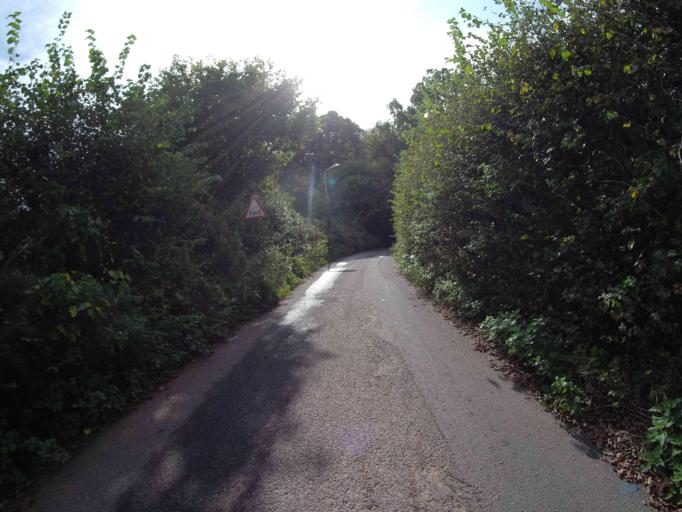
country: GB
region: England
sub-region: Devon
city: Budleigh Salterton
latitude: 50.6322
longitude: -3.3354
